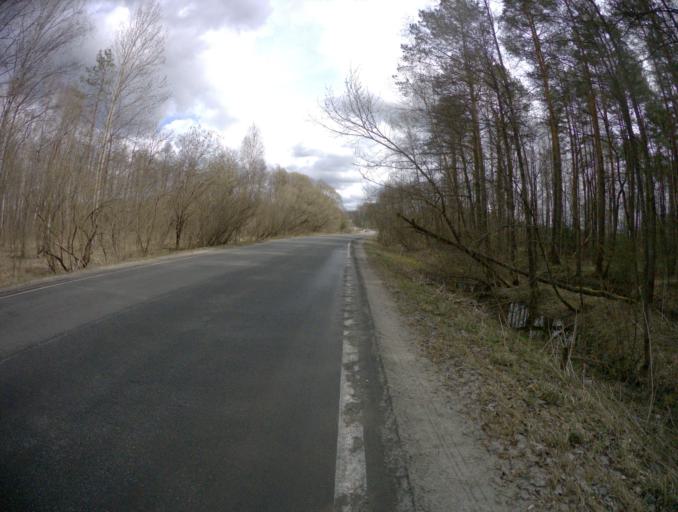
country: RU
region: Vladimir
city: Sudogda
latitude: 56.0746
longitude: 40.7762
